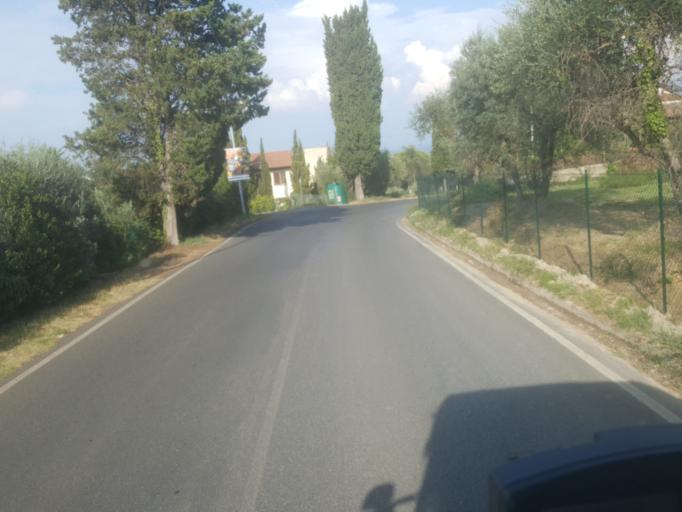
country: IT
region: Tuscany
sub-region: Province of Florence
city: Gambassi Terme
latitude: 43.5332
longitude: 10.9467
